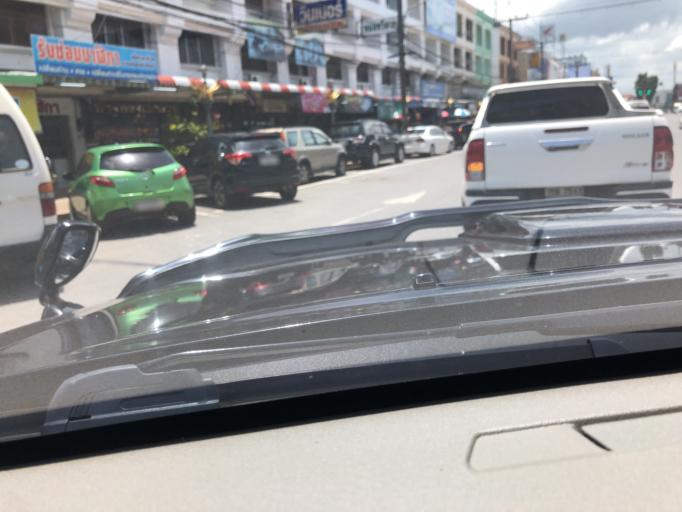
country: TH
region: Krabi
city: Krabi
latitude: 8.0634
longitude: 98.9156
